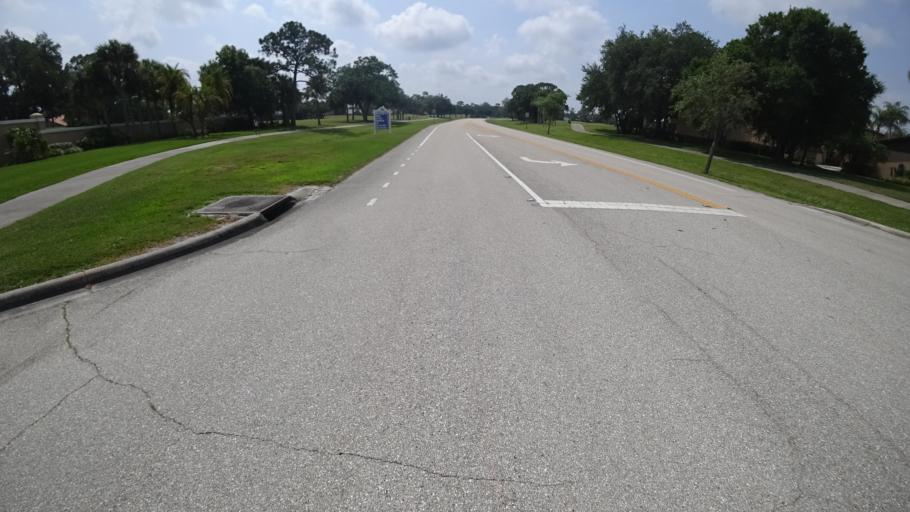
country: US
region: Florida
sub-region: Sarasota County
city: Desoto Lakes
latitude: 27.4096
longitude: -82.4882
